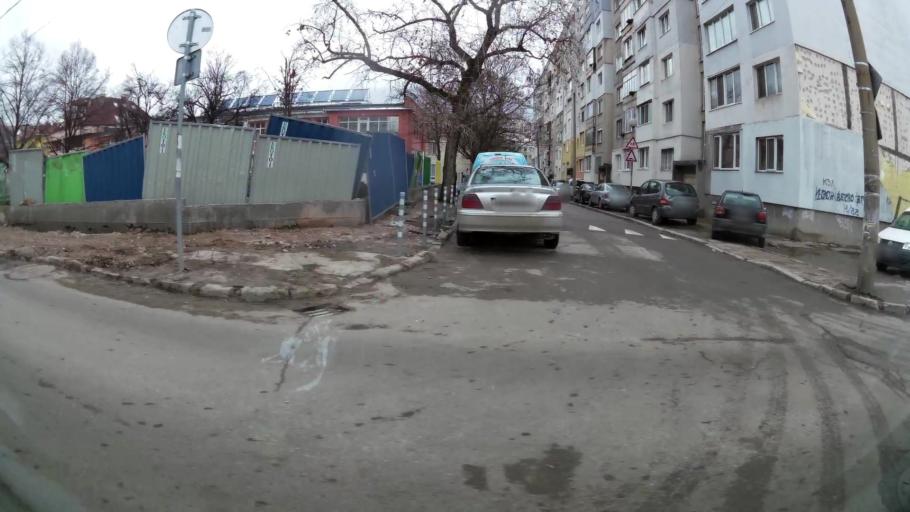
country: BG
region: Sofia-Capital
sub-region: Stolichna Obshtina
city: Sofia
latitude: 42.7250
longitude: 23.2999
